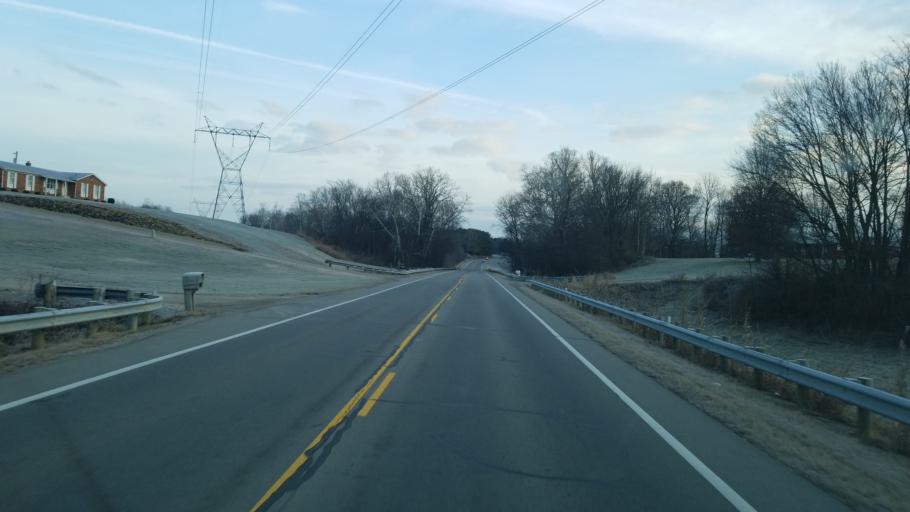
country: US
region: Ohio
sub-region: Ross County
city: North Fork Village
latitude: 39.3289
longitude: -83.0997
